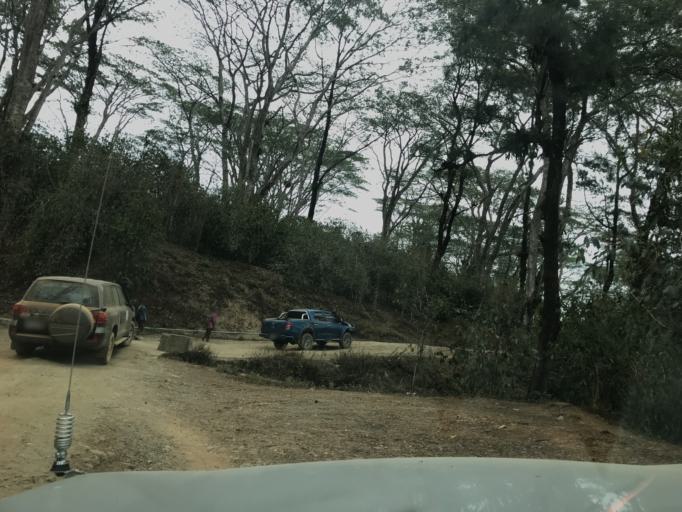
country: TL
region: Ermera
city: Gleno
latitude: -8.8361
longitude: 125.4468
